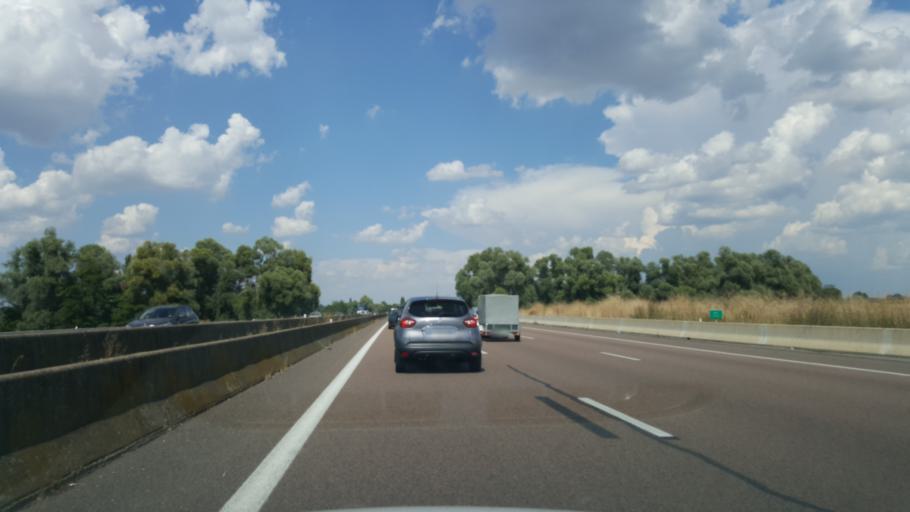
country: FR
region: Bourgogne
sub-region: Departement de Saone-et-Loire
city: Demigny
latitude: 46.9318
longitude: 4.8218
